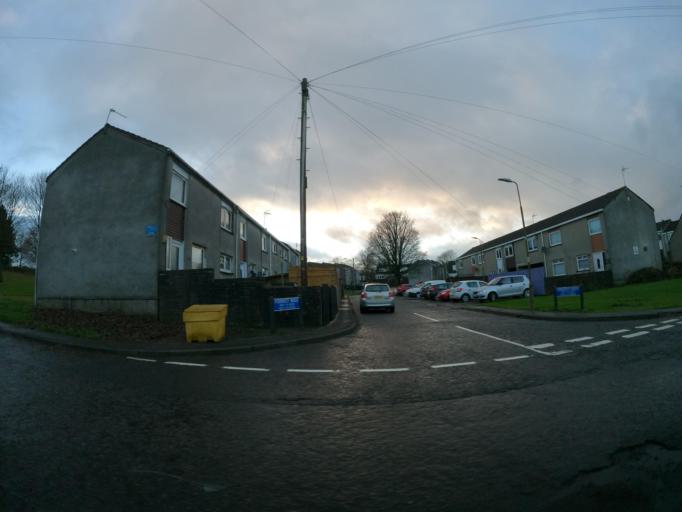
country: GB
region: Scotland
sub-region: West Lothian
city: Livingston
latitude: 55.9258
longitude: -3.5065
